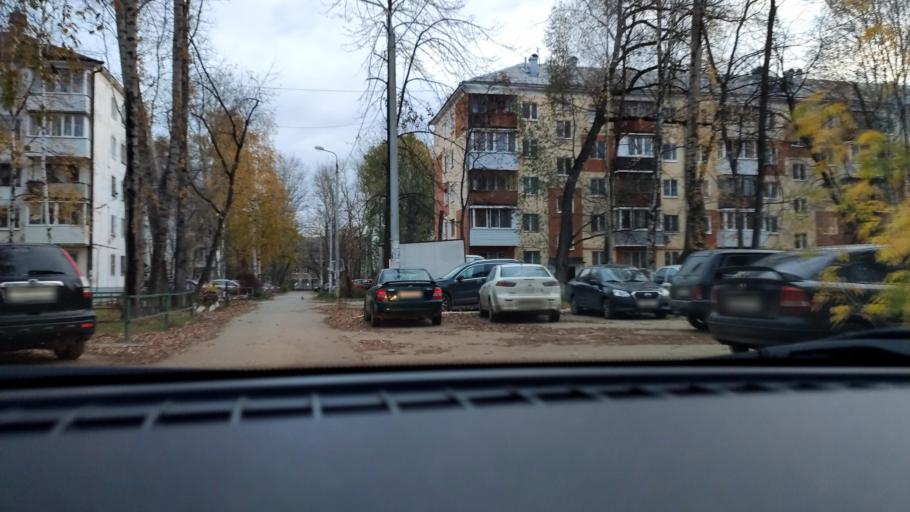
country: RU
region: Perm
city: Perm
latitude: 58.0101
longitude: 56.2882
